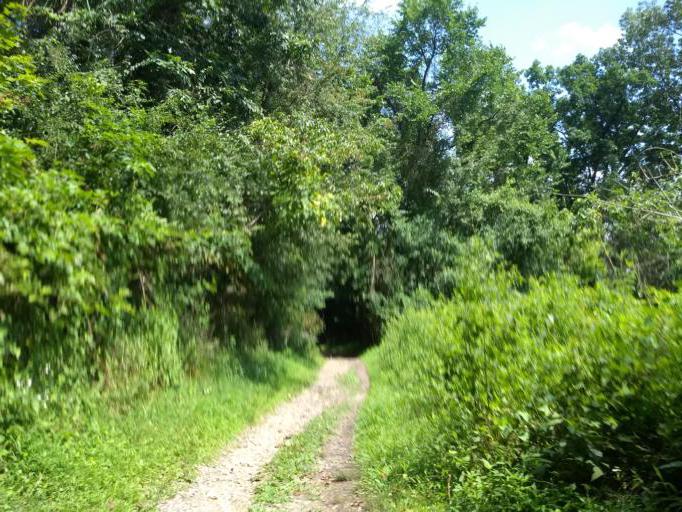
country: US
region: Pennsylvania
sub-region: Allegheny County
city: Swissvale
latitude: 40.4304
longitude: -79.9055
